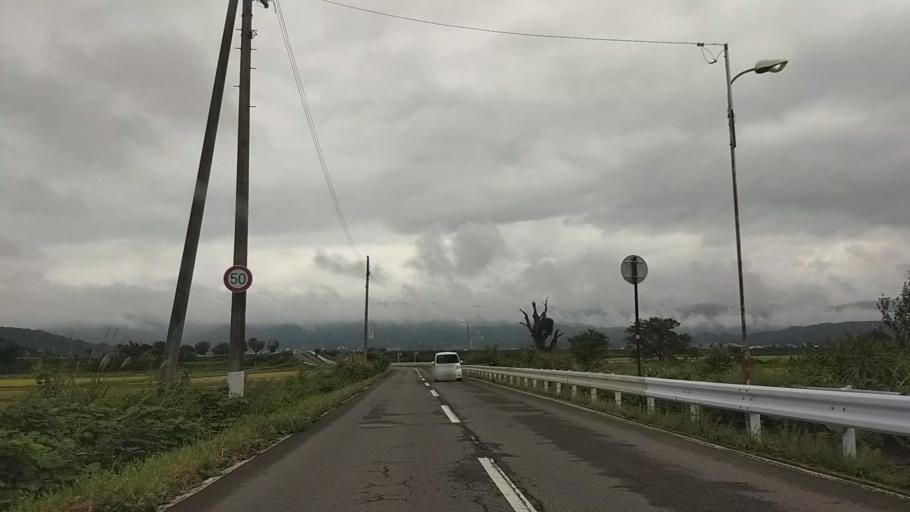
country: JP
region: Nagano
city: Iiyama
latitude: 36.8476
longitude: 138.3977
